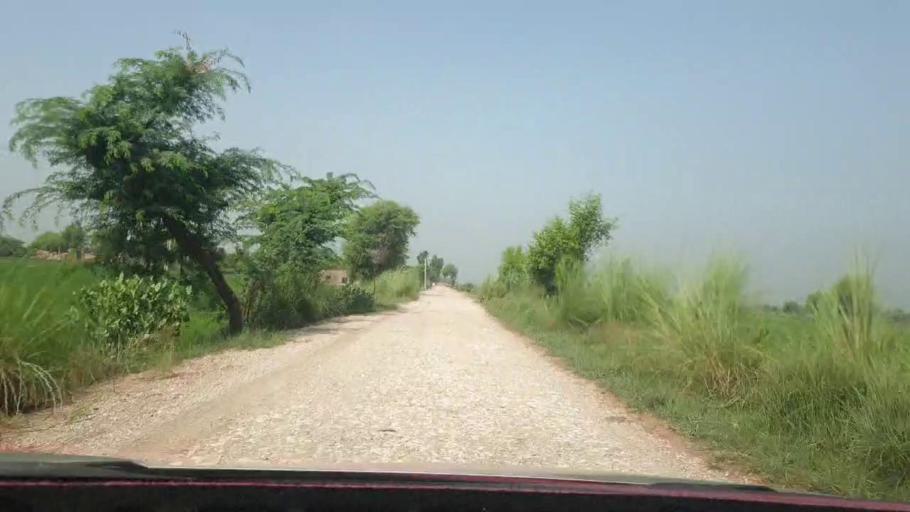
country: PK
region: Sindh
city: Nasirabad
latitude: 27.4304
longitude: 67.8791
